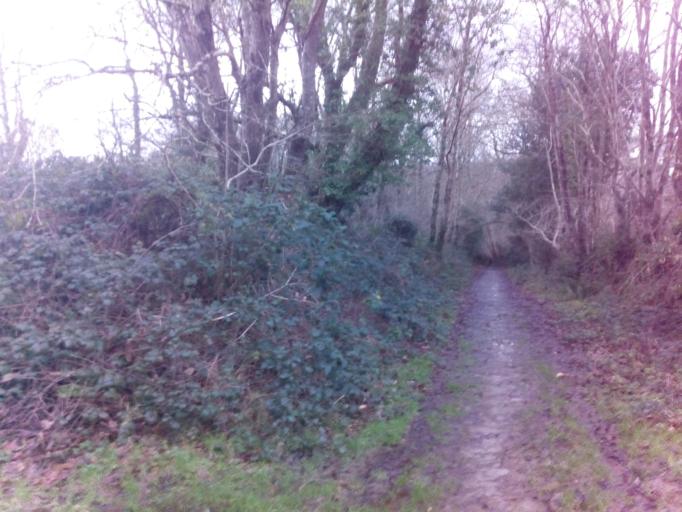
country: FR
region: Brittany
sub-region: Departement du Finistere
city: Loperhet
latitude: 48.3733
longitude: -4.2979
